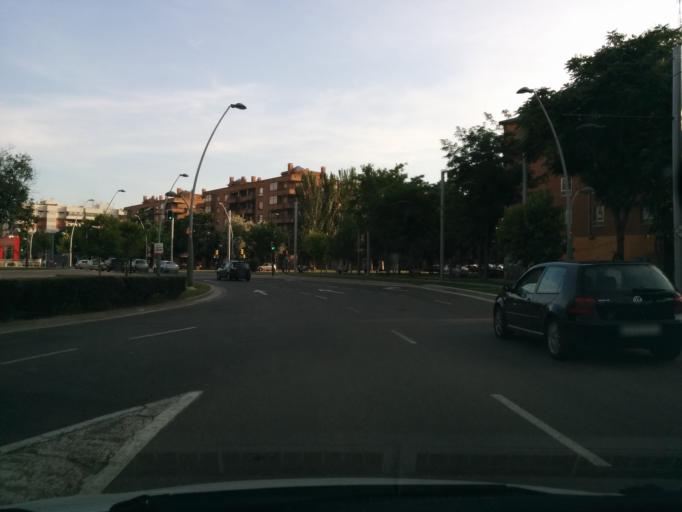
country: ES
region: Aragon
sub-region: Provincia de Zaragoza
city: Almozara
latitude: 41.6788
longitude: -0.8903
